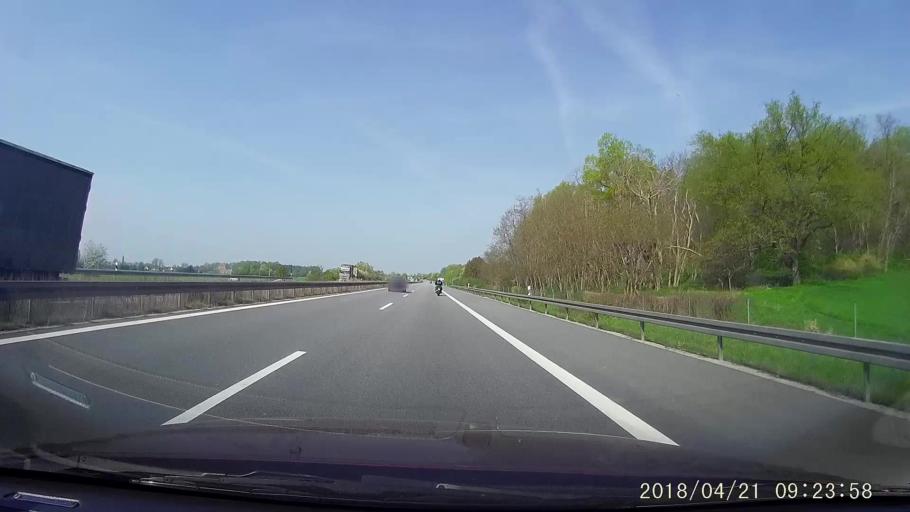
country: DE
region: Saxony
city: Malschwitz
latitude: 51.2068
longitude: 14.5135
